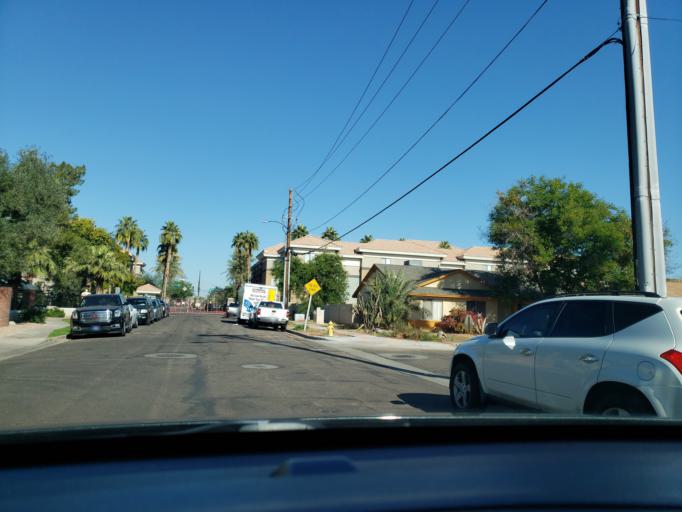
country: US
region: Arizona
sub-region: Maricopa County
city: Phoenix
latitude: 33.4497
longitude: -112.0621
